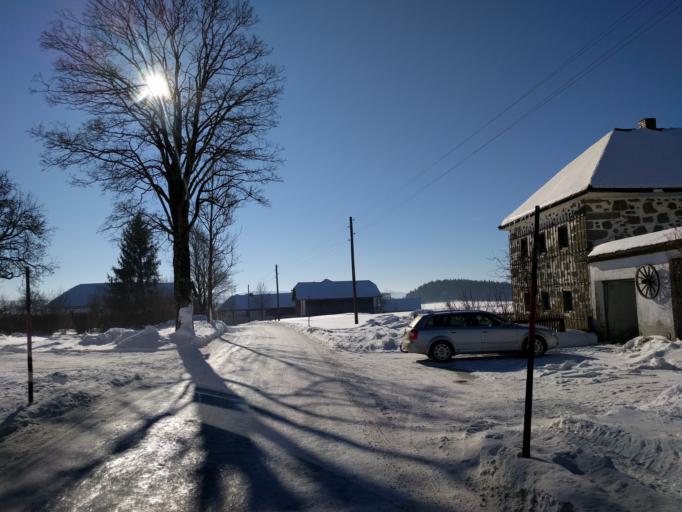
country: AT
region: Upper Austria
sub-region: Politischer Bezirk Urfahr-Umgebung
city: Zwettl an der Rodl
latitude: 48.4860
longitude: 14.2781
